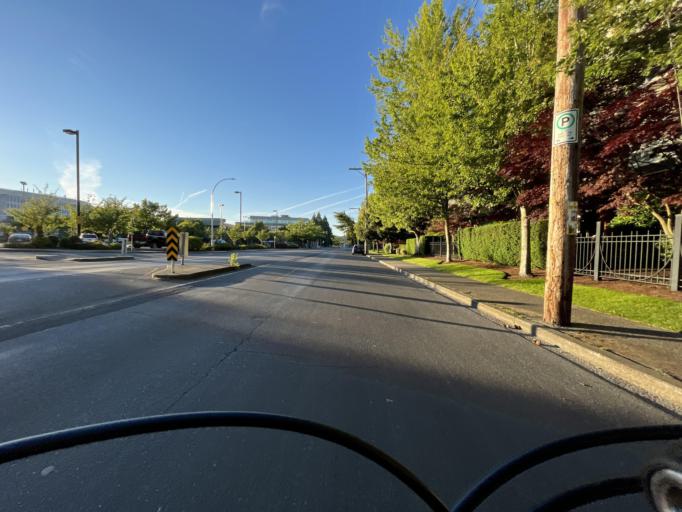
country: CA
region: British Columbia
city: Oak Bay
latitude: 48.4309
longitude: -123.3224
